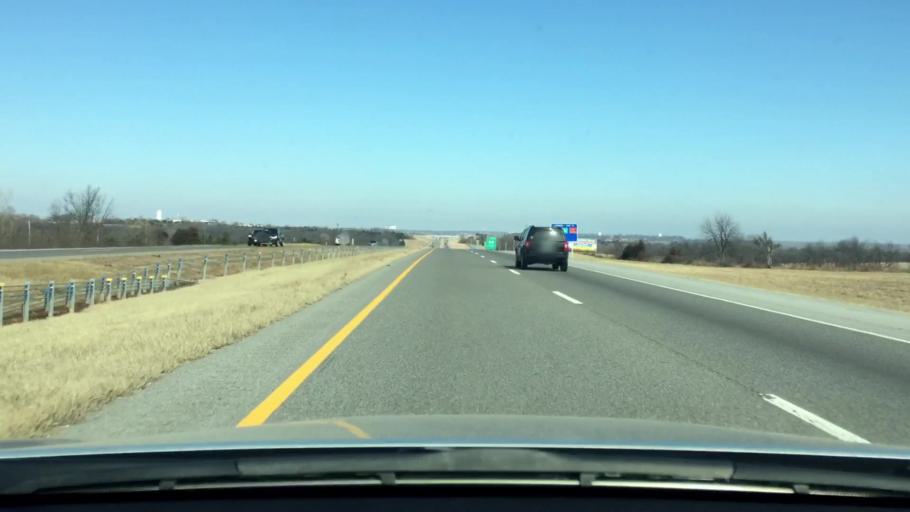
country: US
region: Oklahoma
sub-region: McClain County
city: Purcell
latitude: 34.9622
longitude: -97.3695
